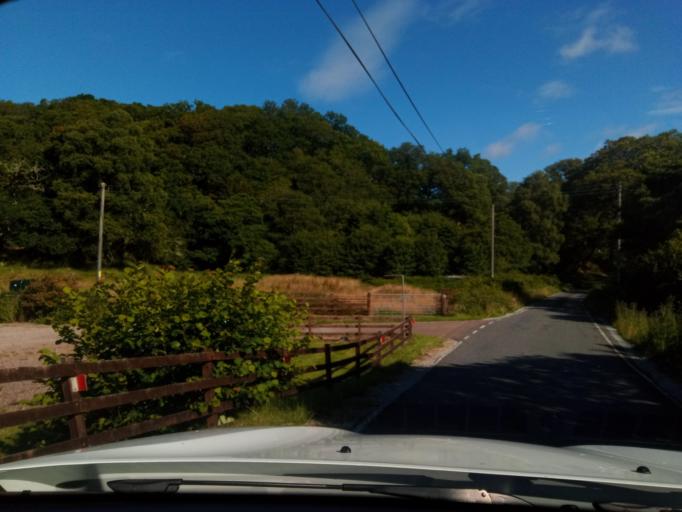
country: GB
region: Scotland
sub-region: Argyll and Bute
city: Isle Of Mull
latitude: 56.6901
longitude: -5.6686
